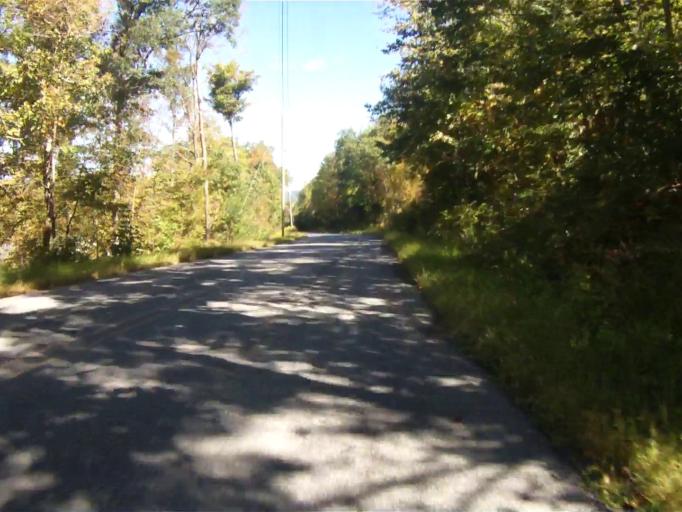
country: US
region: Pennsylvania
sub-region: Centre County
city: Houserville
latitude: 40.8920
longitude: -77.8800
